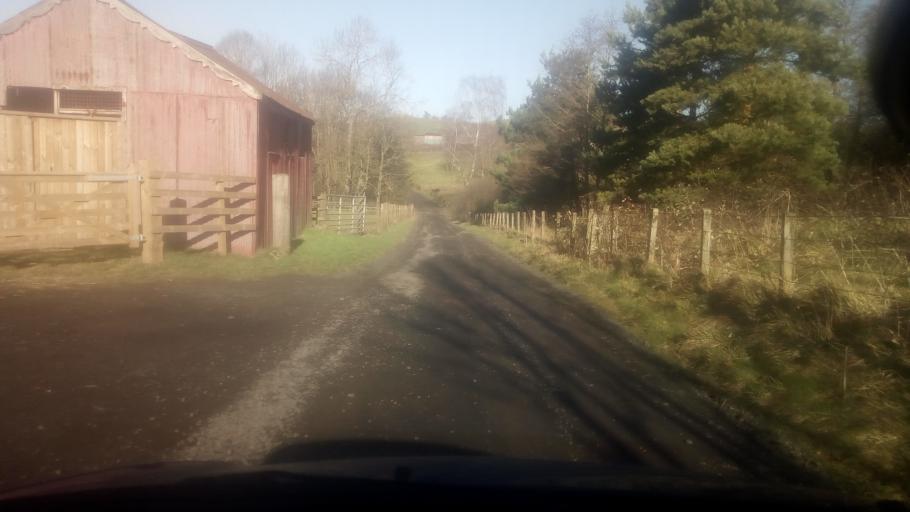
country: GB
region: Scotland
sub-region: The Scottish Borders
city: Jedburgh
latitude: 55.4841
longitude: -2.5355
